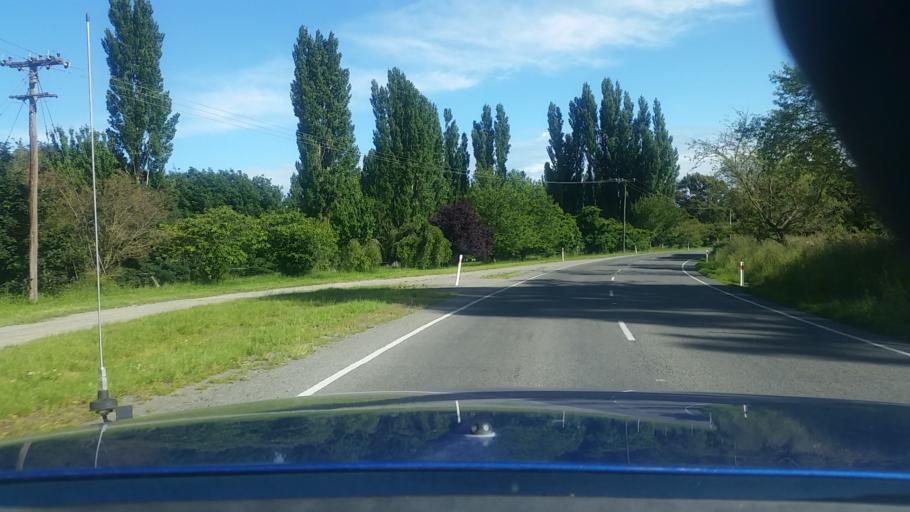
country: NZ
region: Canterbury
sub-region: Ashburton District
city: Ashburton
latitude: -43.8763
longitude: 171.7281
